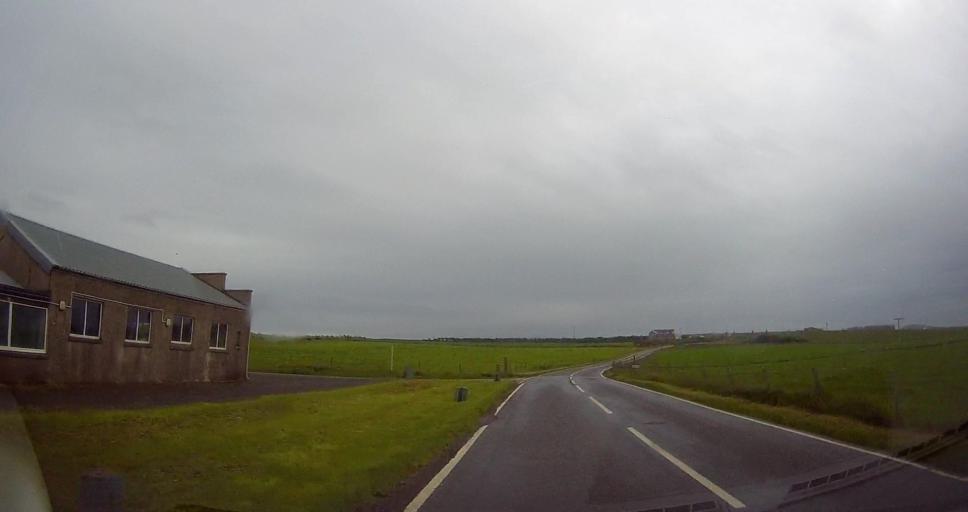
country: GB
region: Scotland
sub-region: Orkney Islands
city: Stromness
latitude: 59.0365
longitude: -3.2827
